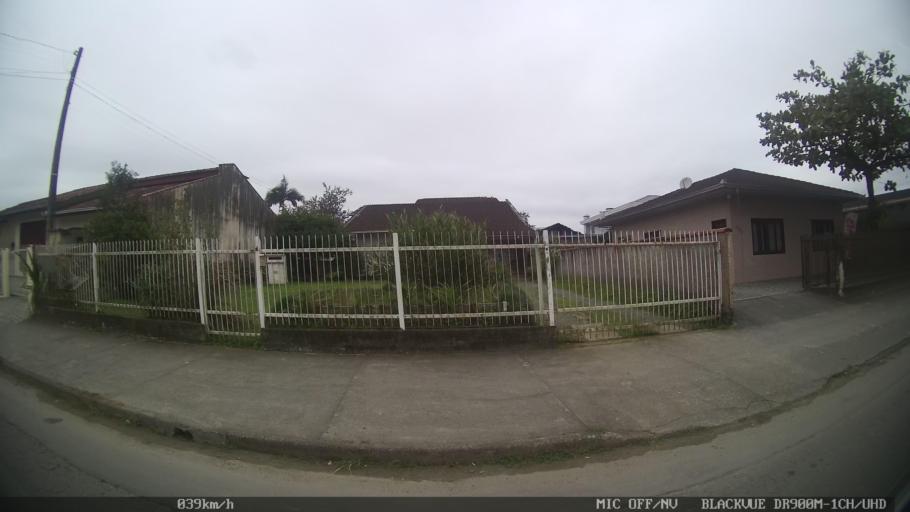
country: BR
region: Santa Catarina
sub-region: Joinville
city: Joinville
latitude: -26.2822
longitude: -48.9069
